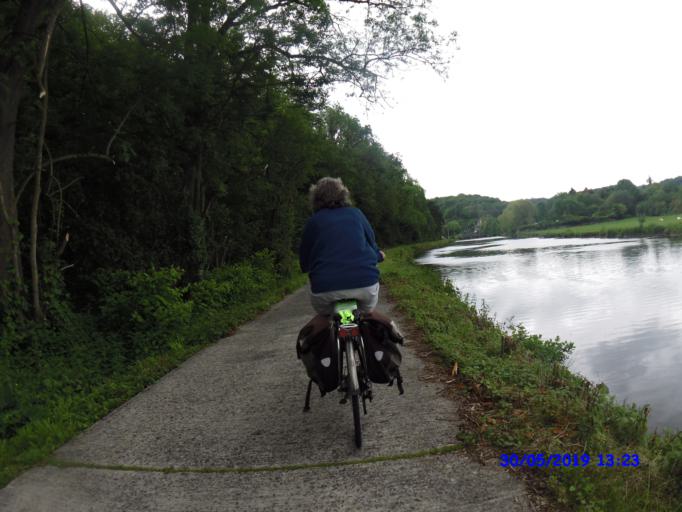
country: BE
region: Wallonia
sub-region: Province du Hainaut
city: Thuin
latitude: 50.3701
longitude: 4.3312
